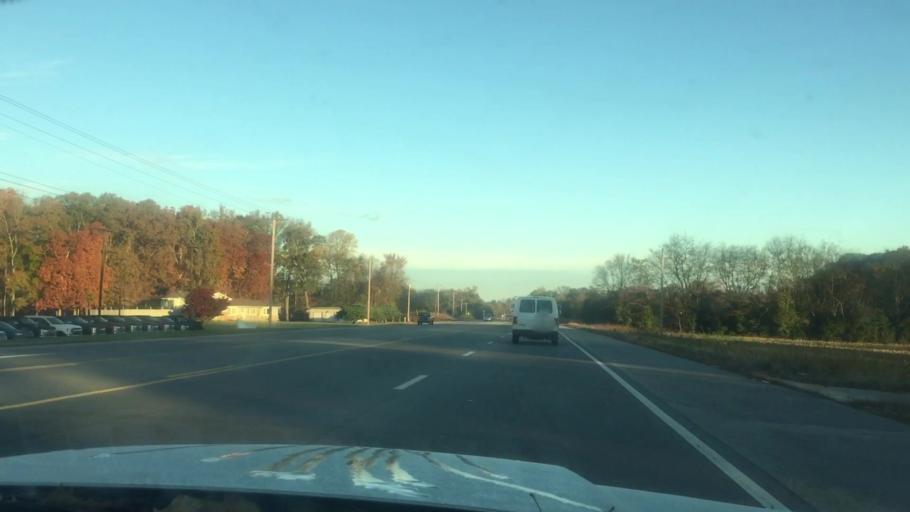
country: US
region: Tennessee
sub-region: Franklin County
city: Estill Springs
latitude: 35.2364
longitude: -86.1117
